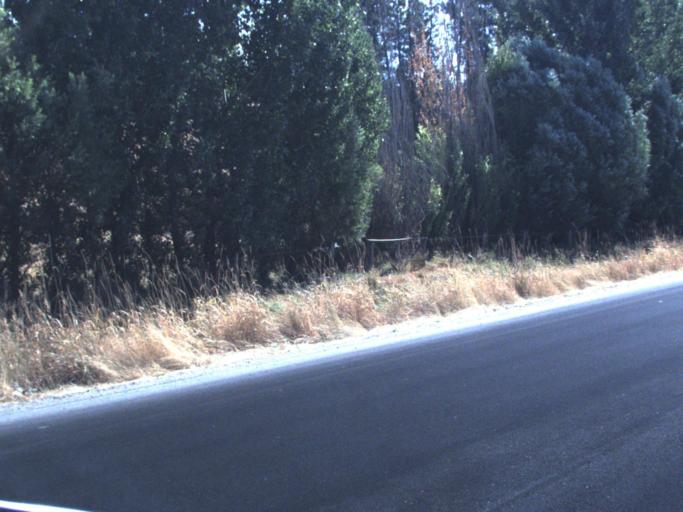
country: US
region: Washington
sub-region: Stevens County
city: Colville
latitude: 48.5015
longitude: -117.9022
